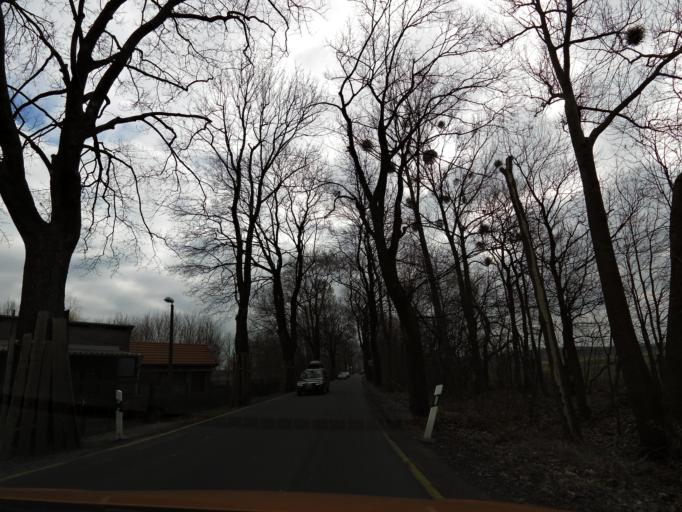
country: DE
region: Brandenburg
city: Werder
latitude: 52.4478
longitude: 12.9814
